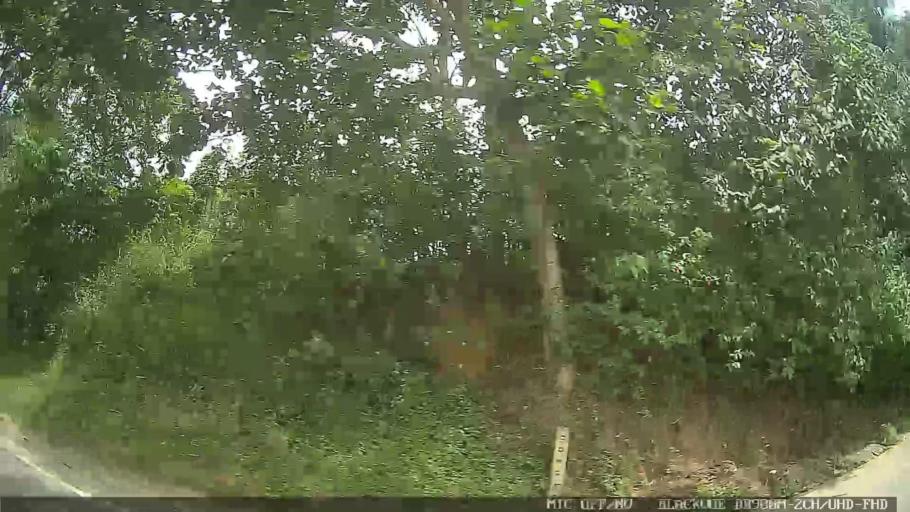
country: BR
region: Sao Paulo
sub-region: Ribeirao Pires
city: Ribeirao Pires
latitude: -23.6526
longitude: -46.3276
